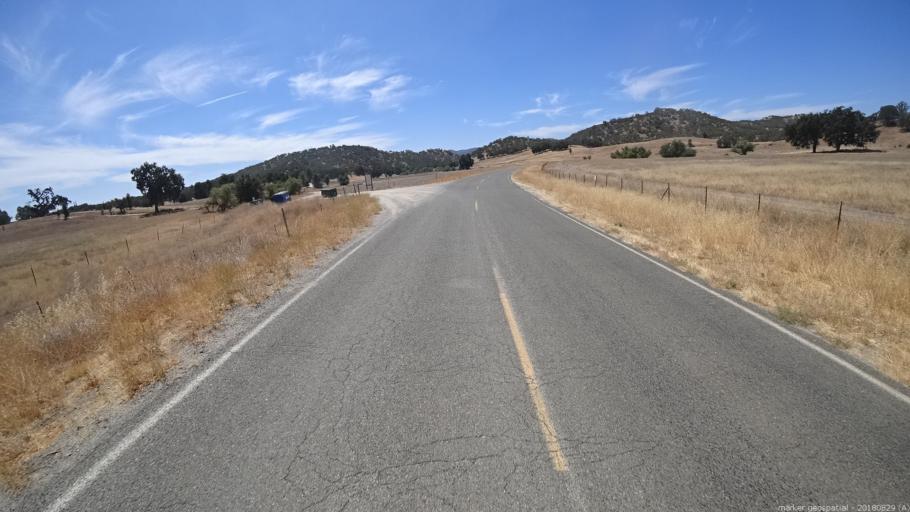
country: US
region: California
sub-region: San Luis Obispo County
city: Lake Nacimiento
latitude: 35.9234
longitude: -121.0823
